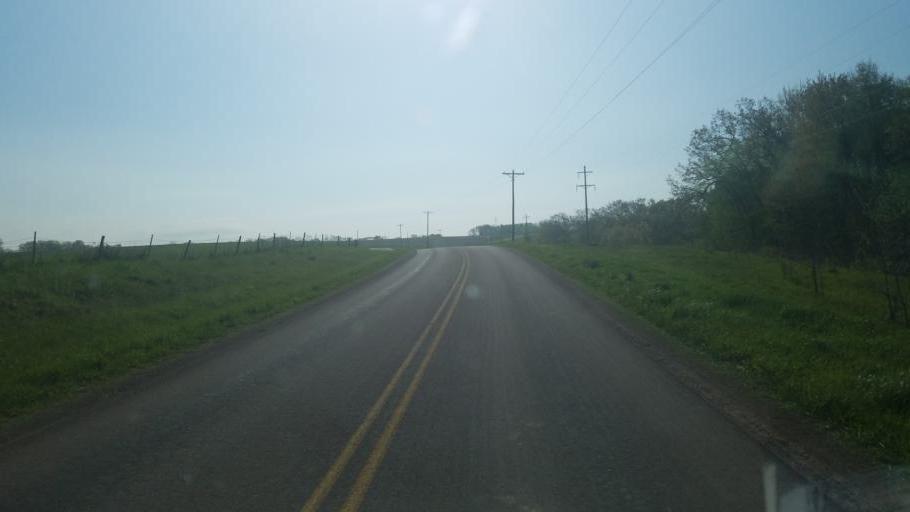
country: US
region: Wisconsin
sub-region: Vernon County
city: Hillsboro
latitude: 43.5950
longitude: -90.4015
